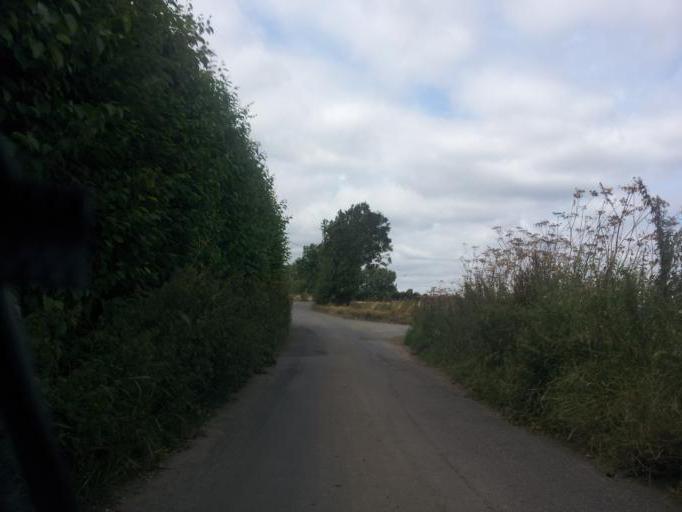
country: GB
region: England
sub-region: Kent
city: Newington
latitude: 51.3076
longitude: 0.6595
